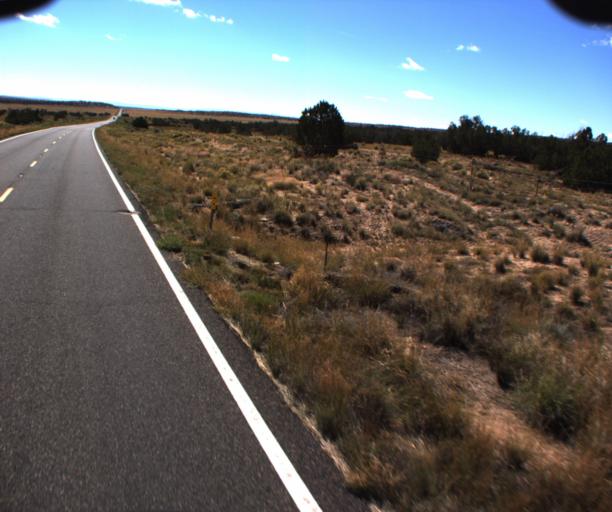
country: US
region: Arizona
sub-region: Apache County
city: Saint Johns
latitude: 34.7814
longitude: -109.2385
